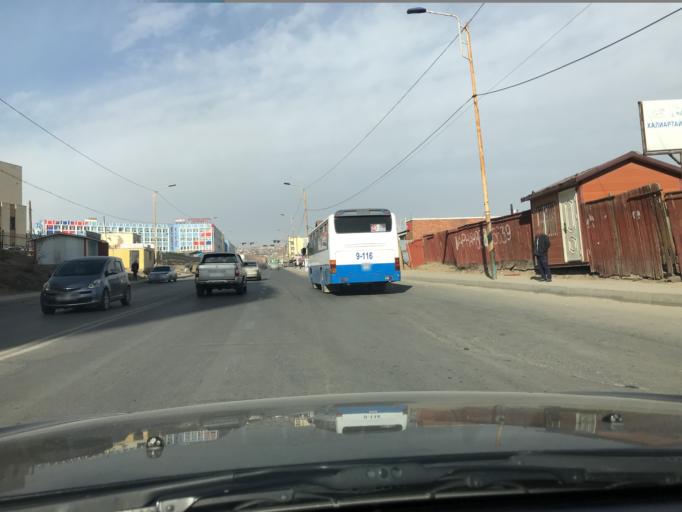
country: MN
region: Ulaanbaatar
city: Ulaanbaatar
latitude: 47.9270
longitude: 106.8935
